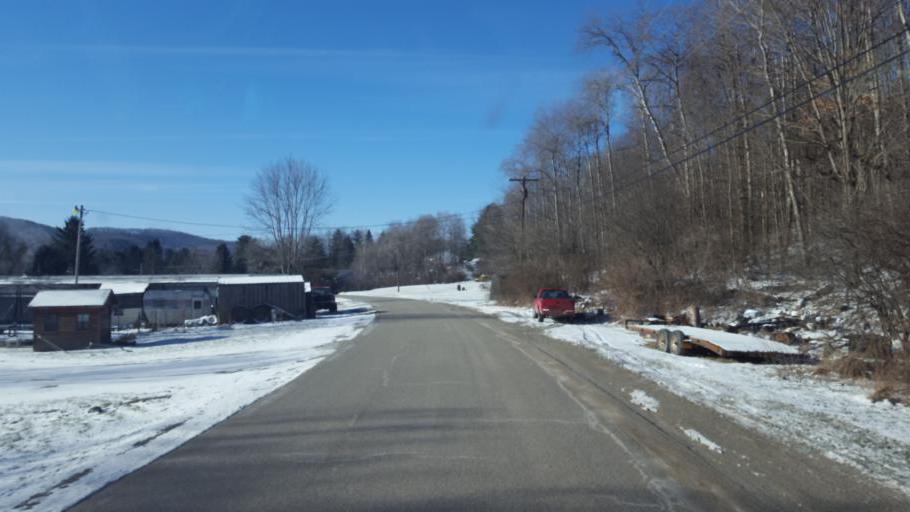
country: US
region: New York
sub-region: Allegany County
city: Wellsville
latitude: 42.1374
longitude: -77.9140
